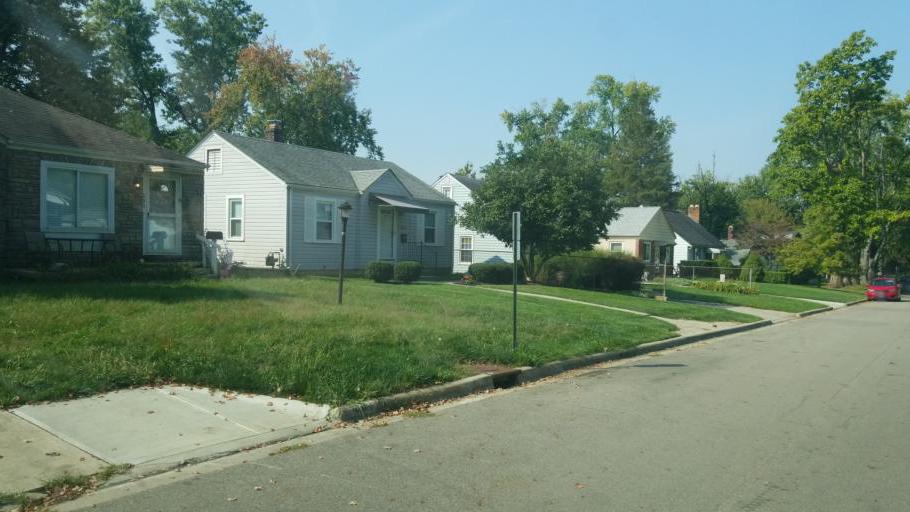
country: US
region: Ohio
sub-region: Franklin County
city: Worthington
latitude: 40.0723
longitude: -83.0244
